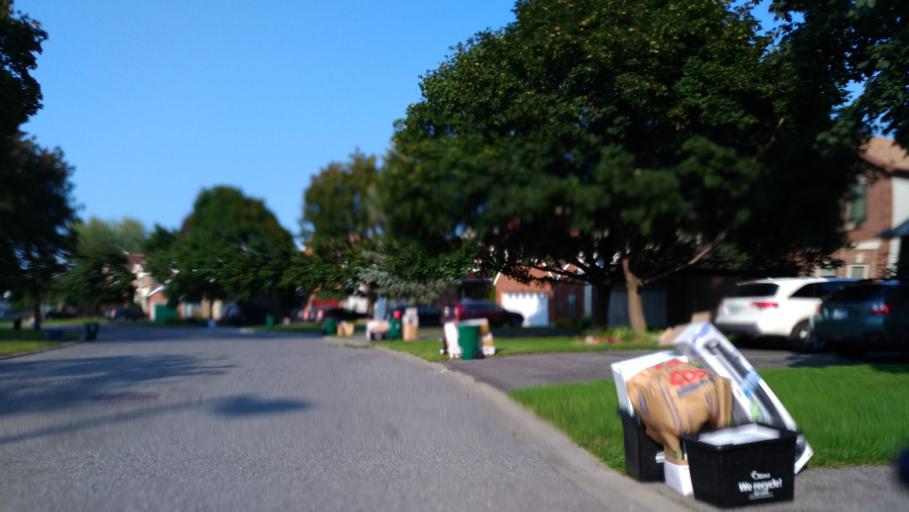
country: CA
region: Ontario
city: Bells Corners
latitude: 45.3470
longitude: -75.9294
